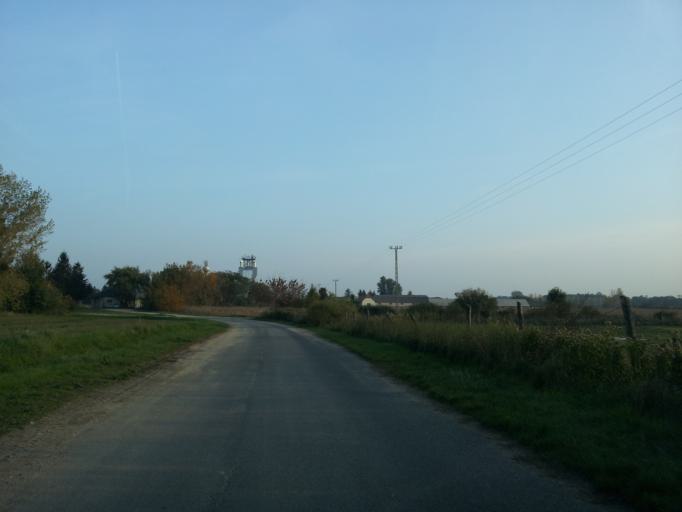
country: HU
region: Komarom-Esztergom
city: Kisber
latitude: 47.4681
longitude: 17.9550
